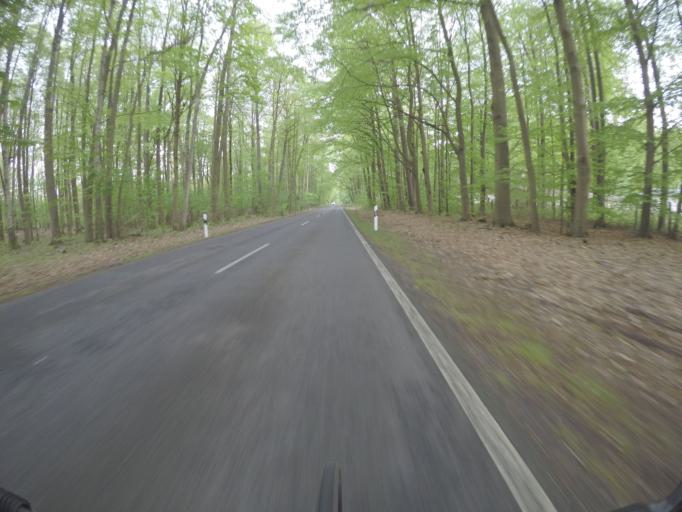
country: DE
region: Brandenburg
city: Joachimsthal
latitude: 52.9256
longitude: 13.7326
